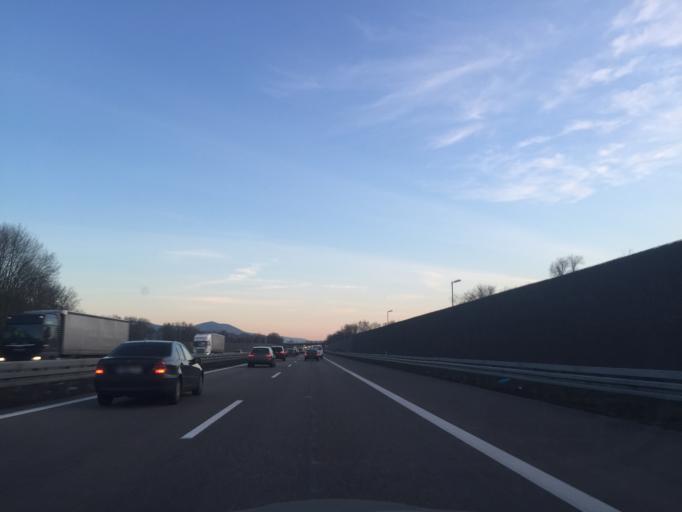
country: DE
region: Baden-Wuerttemberg
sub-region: Karlsruhe Region
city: Weinheim
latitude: 49.5339
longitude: 8.6322
